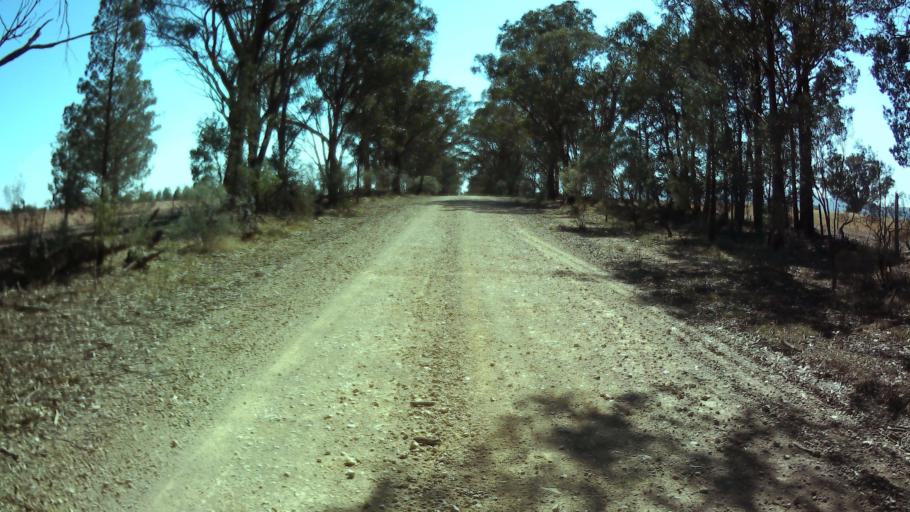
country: AU
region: New South Wales
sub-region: Weddin
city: Grenfell
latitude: -33.9058
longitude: 147.8552
